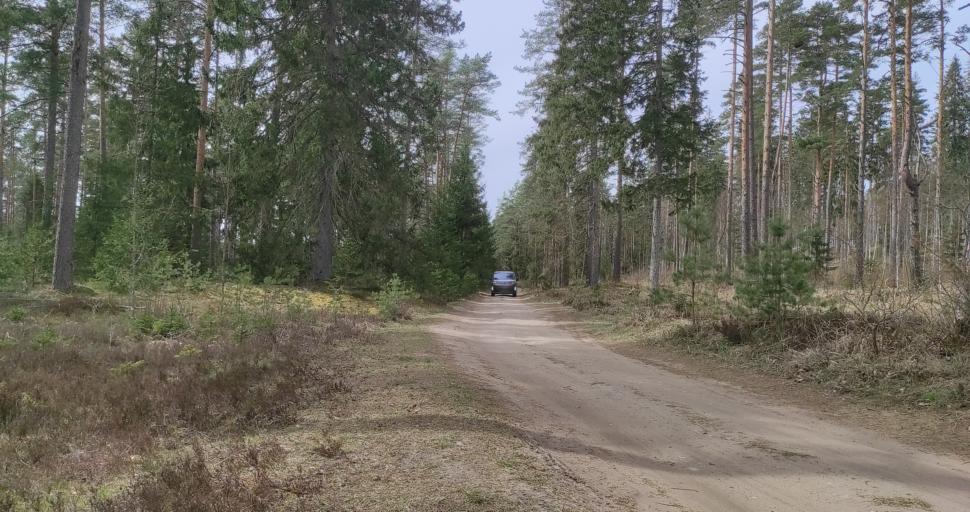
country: LV
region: Talsu Rajons
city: Stende
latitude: 57.0842
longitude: 22.3857
